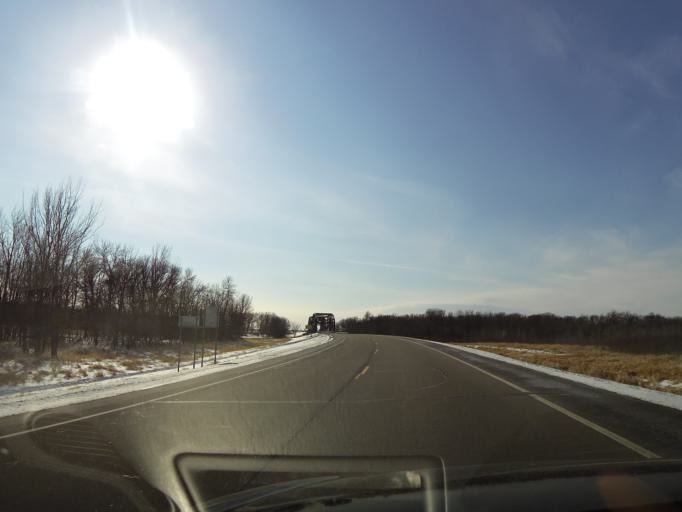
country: US
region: North Dakota
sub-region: Walsh County
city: Grafton
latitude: 48.4146
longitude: -97.1343
